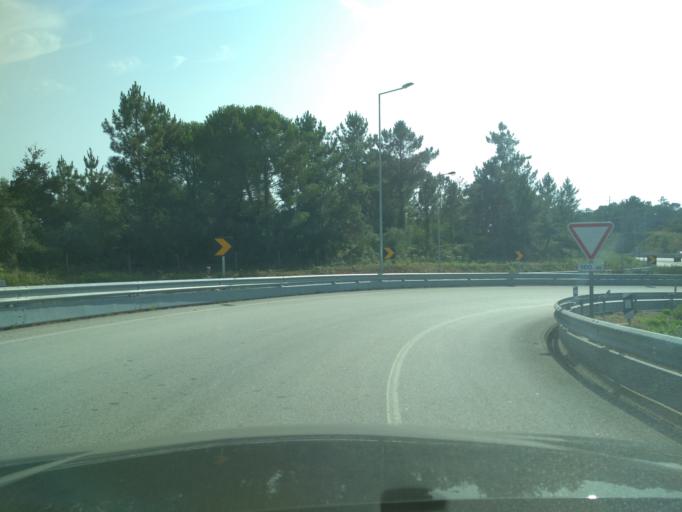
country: PT
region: Coimbra
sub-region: Condeixa-A-Nova
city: Condeixa-a-Nova
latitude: 40.1273
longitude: -8.4843
